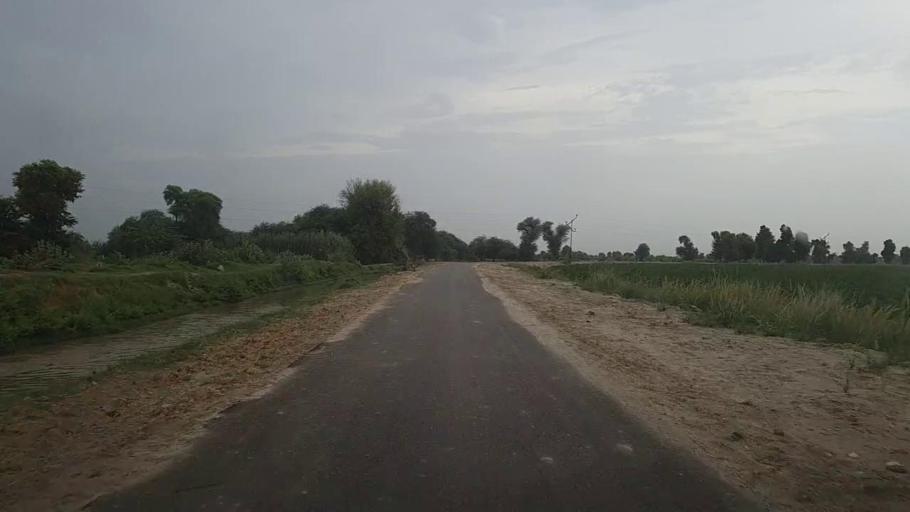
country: PK
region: Sindh
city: Karaundi
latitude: 26.9634
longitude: 68.3654
